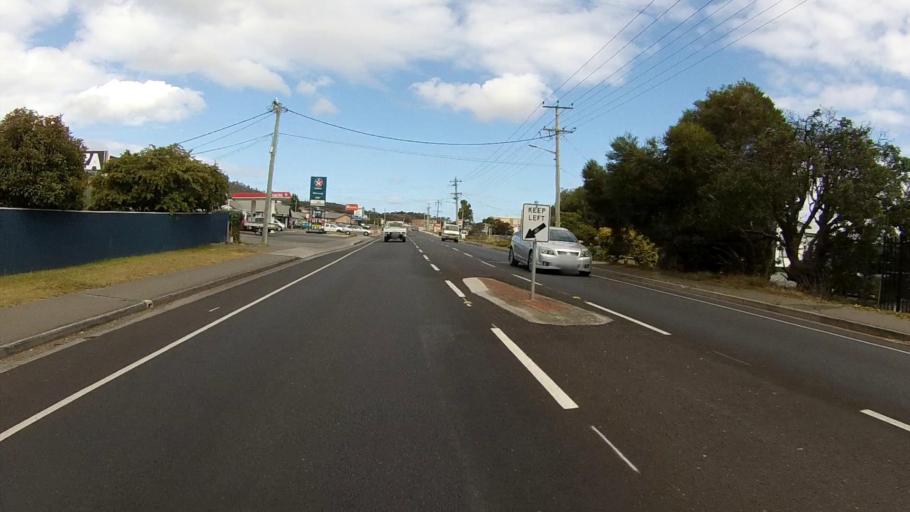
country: AU
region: Tasmania
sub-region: Clarence
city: Rokeby
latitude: -42.9014
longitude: 147.4459
